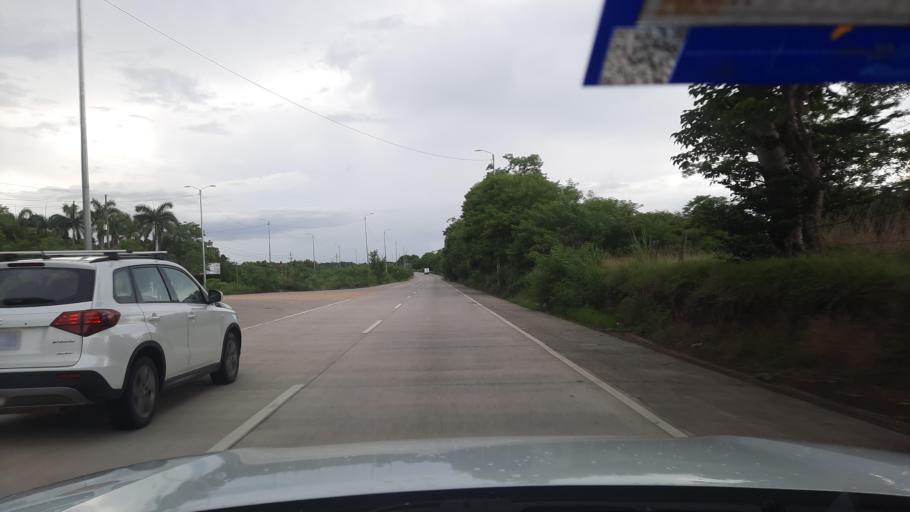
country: CR
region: Guanacaste
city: Bagaces
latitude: 10.5320
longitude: -85.2714
